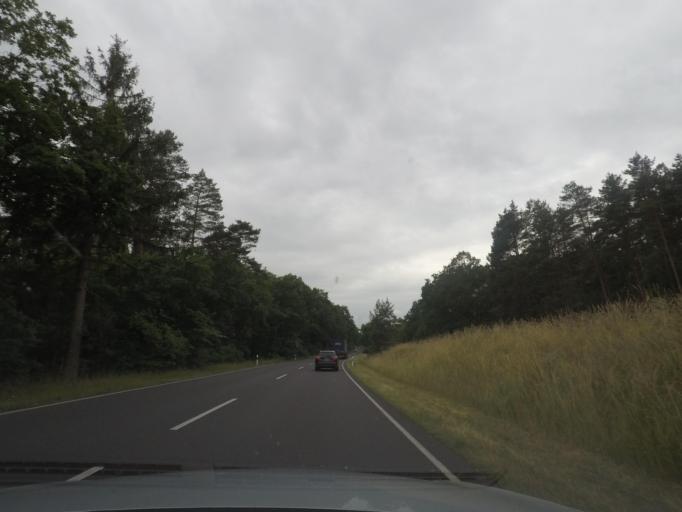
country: DE
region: Saxony-Anhalt
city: Haldensleben I
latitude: 52.3235
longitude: 11.4392
